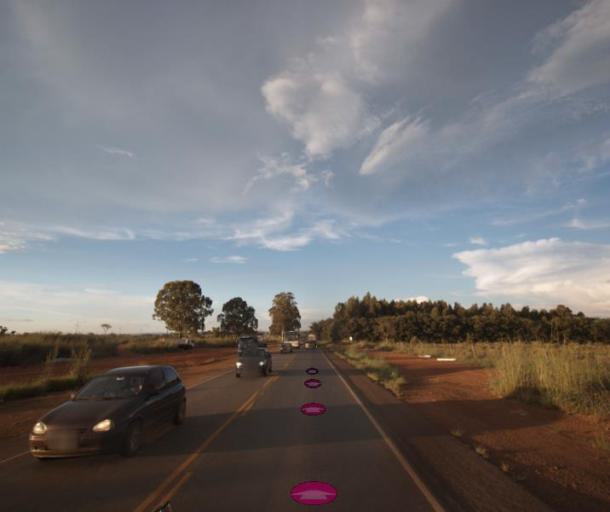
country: BR
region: Goias
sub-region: Anapolis
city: Anapolis
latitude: -16.2225
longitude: -48.9236
